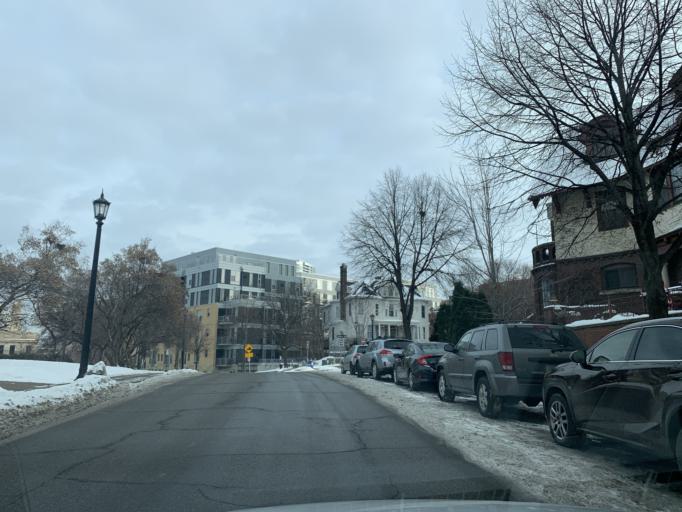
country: US
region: Minnesota
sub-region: Hennepin County
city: Minneapolis
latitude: 44.9667
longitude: -93.2865
